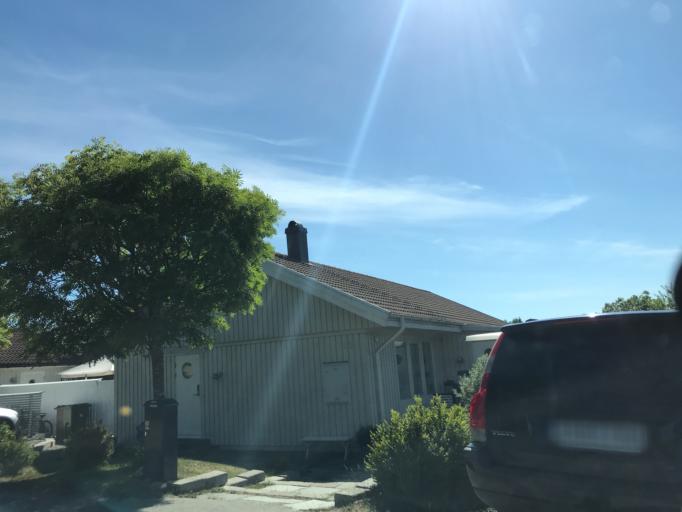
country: SE
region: Stockholm
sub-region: Jarfalla Kommun
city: Jakobsberg
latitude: 59.4549
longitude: 17.8906
